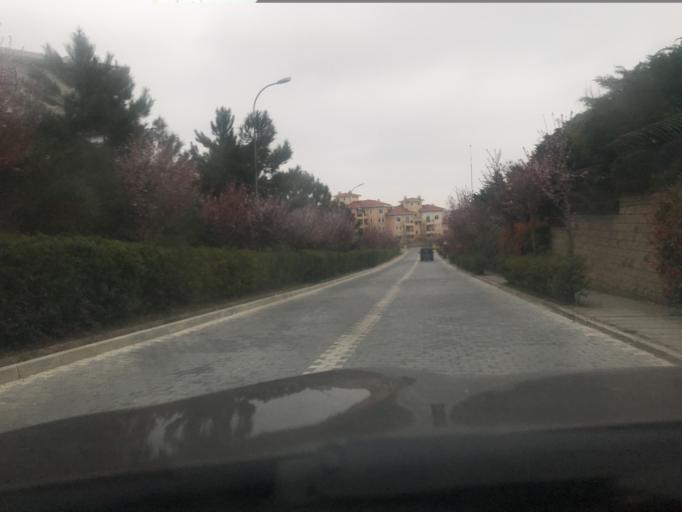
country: TR
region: Istanbul
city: Umraniye
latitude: 41.0412
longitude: 29.1579
